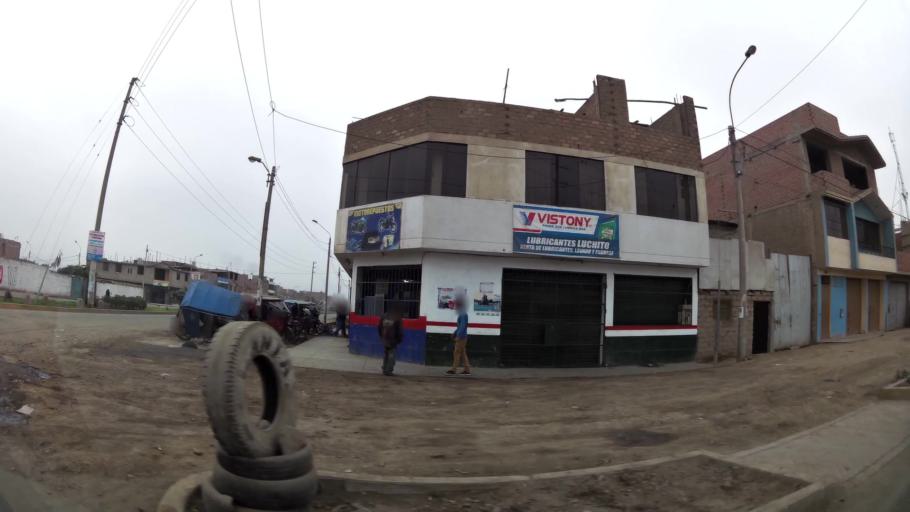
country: PE
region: Lima
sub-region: Lima
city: Urb. Santo Domingo
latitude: -11.8838
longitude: -77.0301
